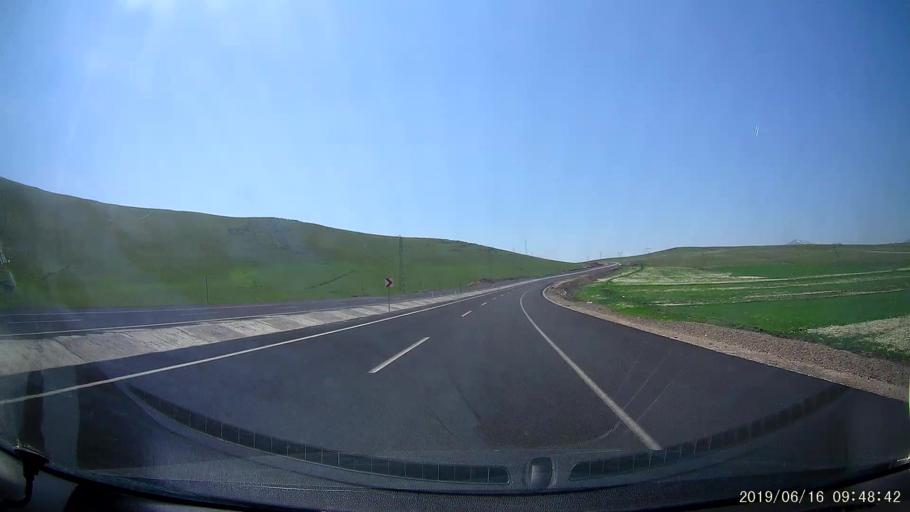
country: TR
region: Kars
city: Digor
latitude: 40.4308
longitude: 43.3551
